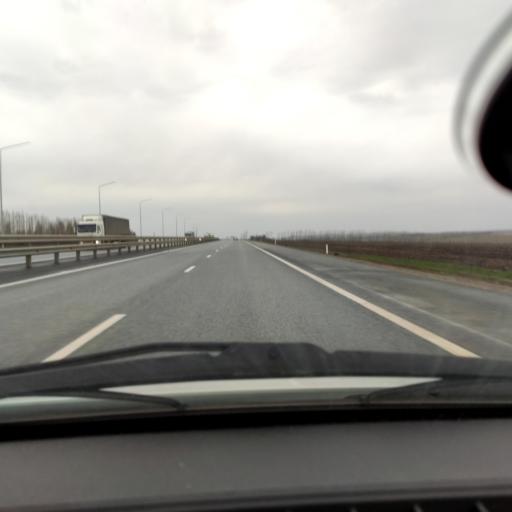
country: RU
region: Bashkortostan
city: Tolbazy
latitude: 54.1647
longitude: 55.9025
